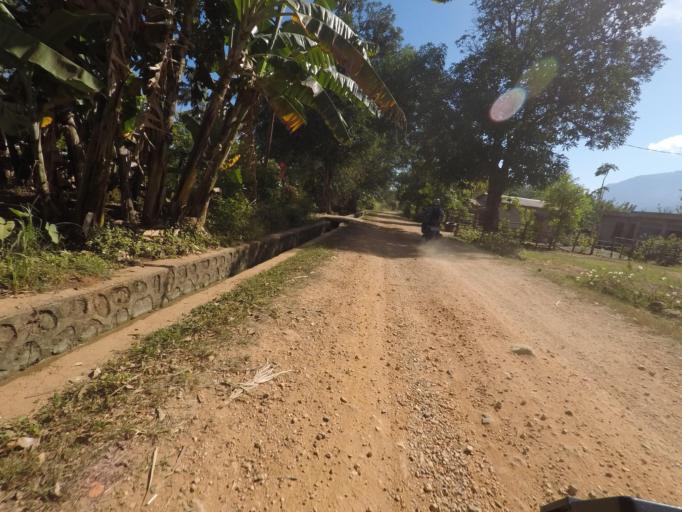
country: TL
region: Bobonaro
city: Maliana
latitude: -8.9627
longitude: 125.2177
